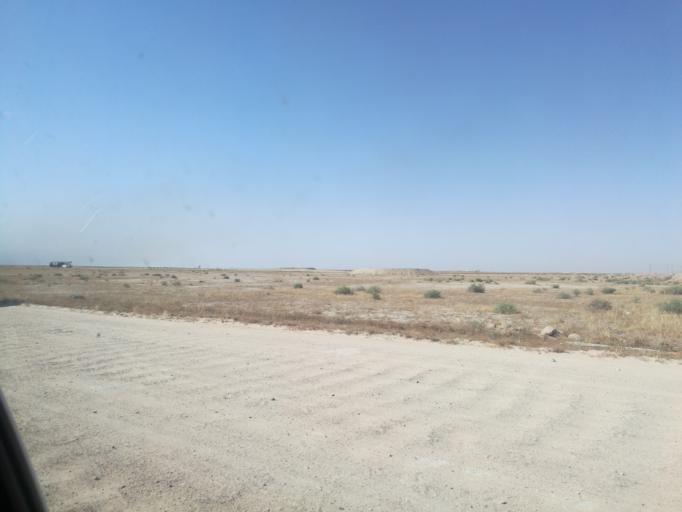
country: IQ
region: Basra Governorate
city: Az Zubayr
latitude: 30.1587
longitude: 47.4282
